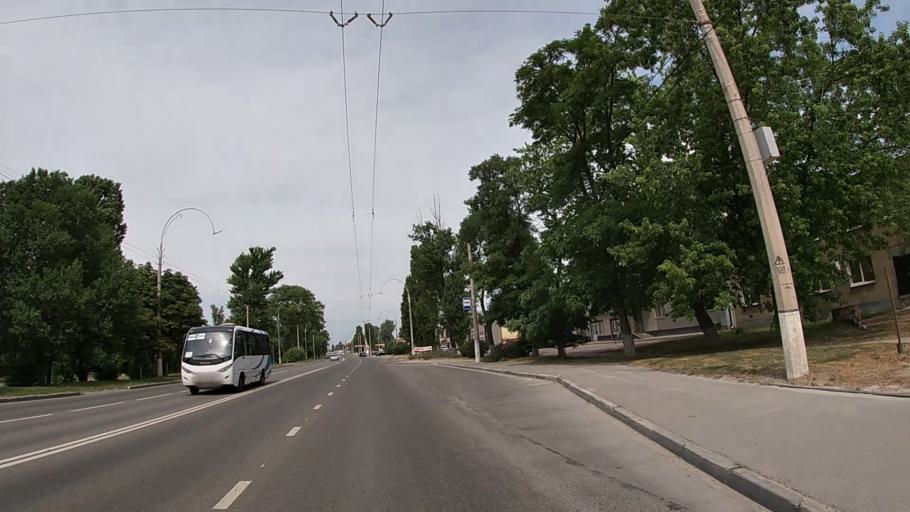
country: RU
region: Belgorod
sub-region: Belgorodskiy Rayon
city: Belgorod
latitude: 50.6093
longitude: 36.5458
